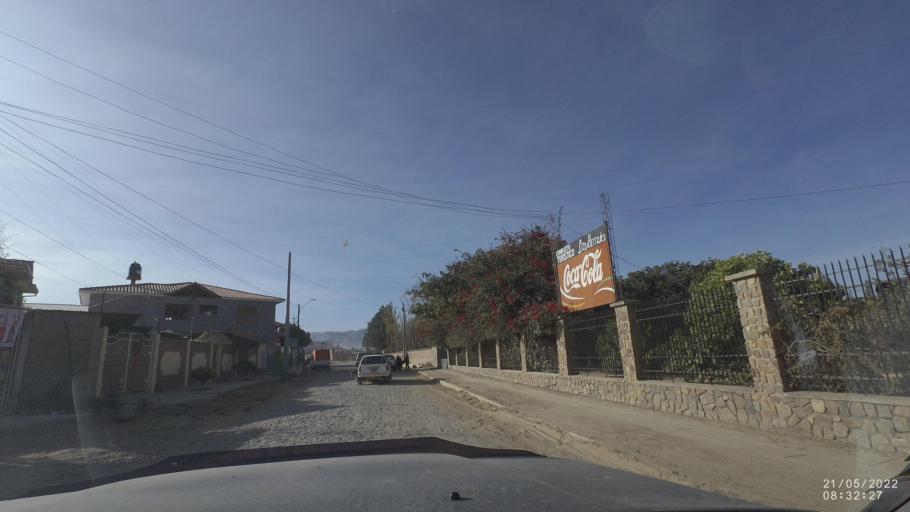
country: BO
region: Cochabamba
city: Cochabamba
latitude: -17.3852
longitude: -66.0535
